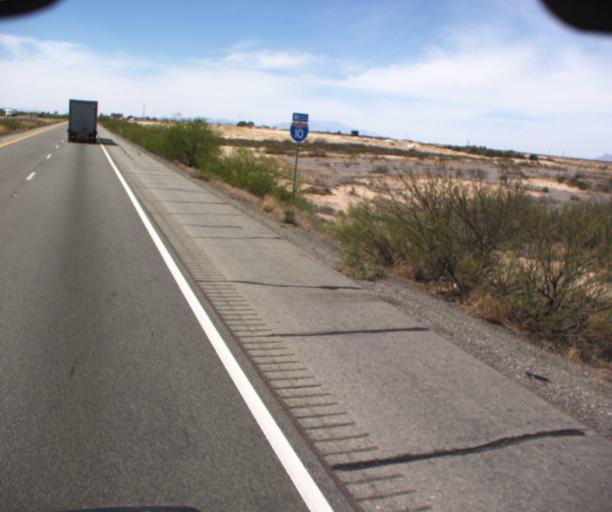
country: US
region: New Mexico
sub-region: Hidalgo County
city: Lordsburg
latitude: 32.2590
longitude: -109.2085
